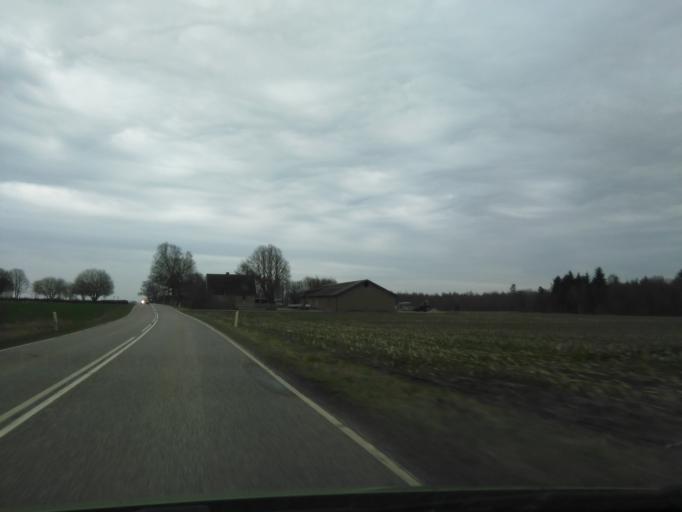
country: DK
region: Central Jutland
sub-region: Randers Kommune
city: Spentrup
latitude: 56.5650
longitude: 9.9993
